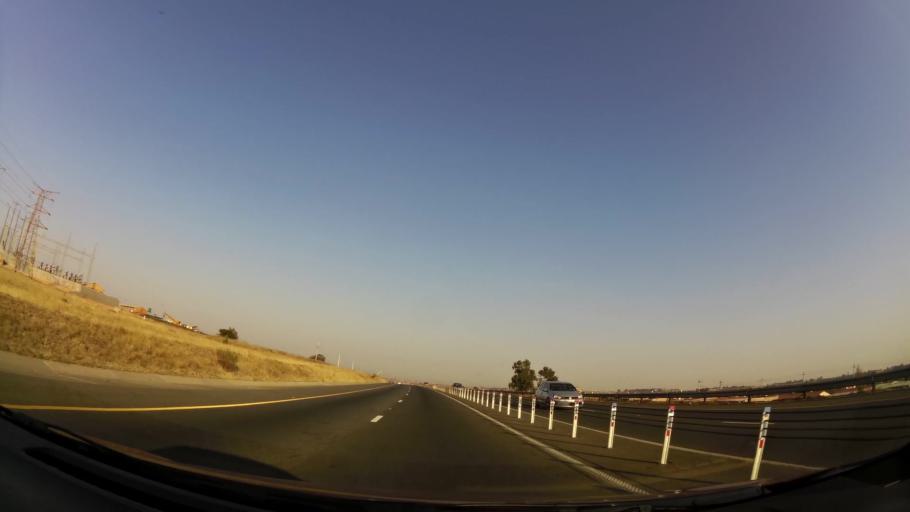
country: ZA
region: Gauteng
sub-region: City of Johannesburg Metropolitan Municipality
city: Roodepoort
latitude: -26.2173
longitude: 27.9488
